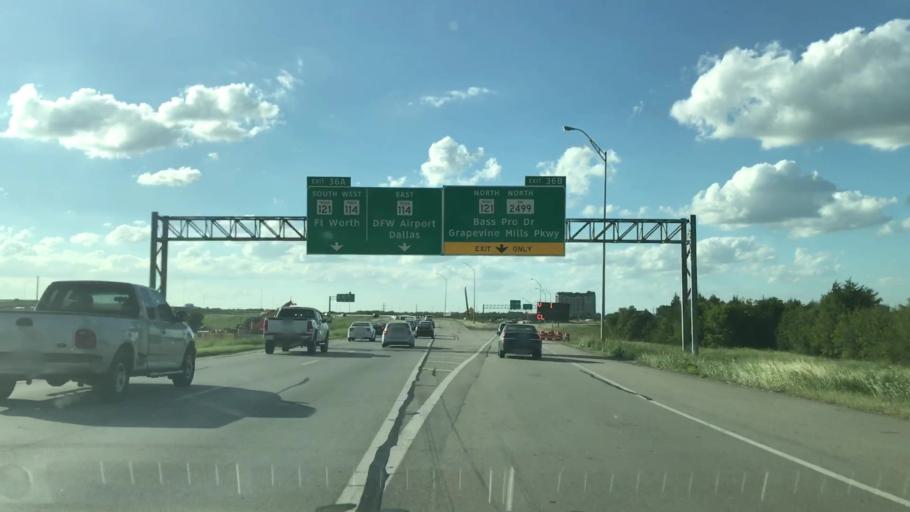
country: US
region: Texas
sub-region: Dallas County
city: Coppell
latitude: 32.9495
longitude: -97.0333
